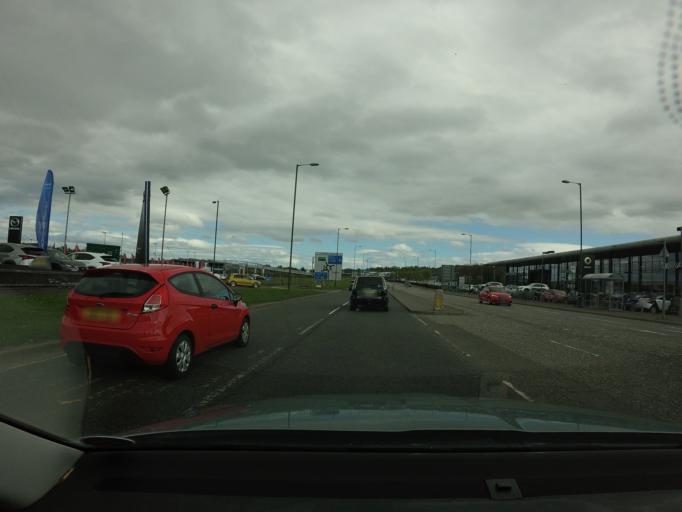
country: GB
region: Scotland
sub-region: Edinburgh
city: Newbridge
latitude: 55.9403
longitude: -3.4068
